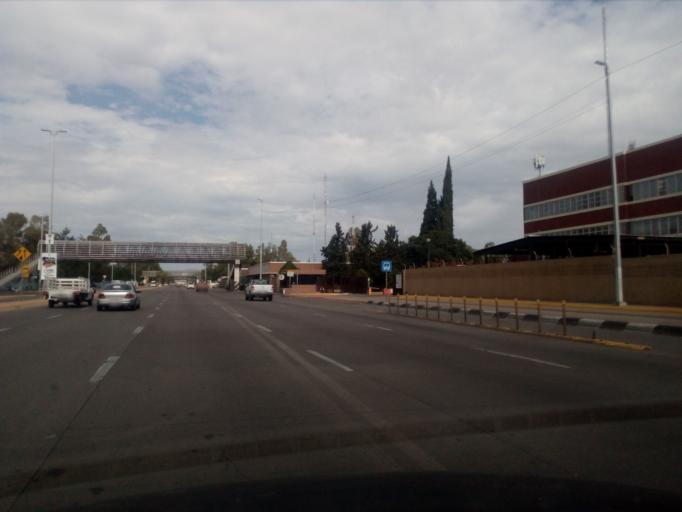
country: MX
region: Durango
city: Victoria de Durango
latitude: 24.0338
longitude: -104.6415
